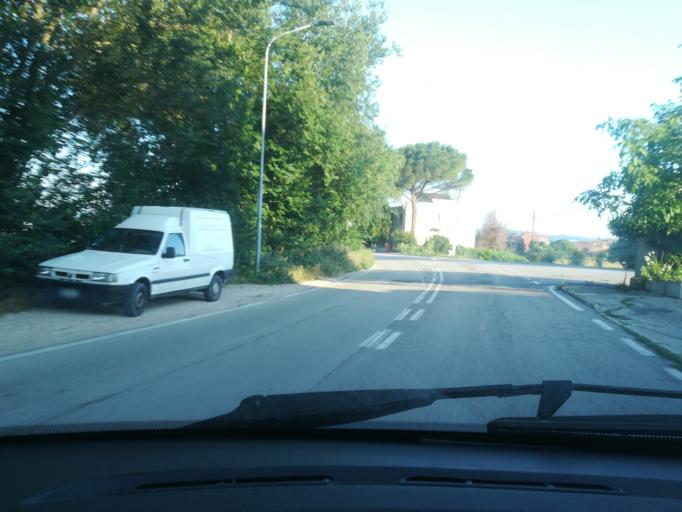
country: IT
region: The Marches
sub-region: Provincia di Macerata
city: Piediripa
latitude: 43.2808
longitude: 13.4822
